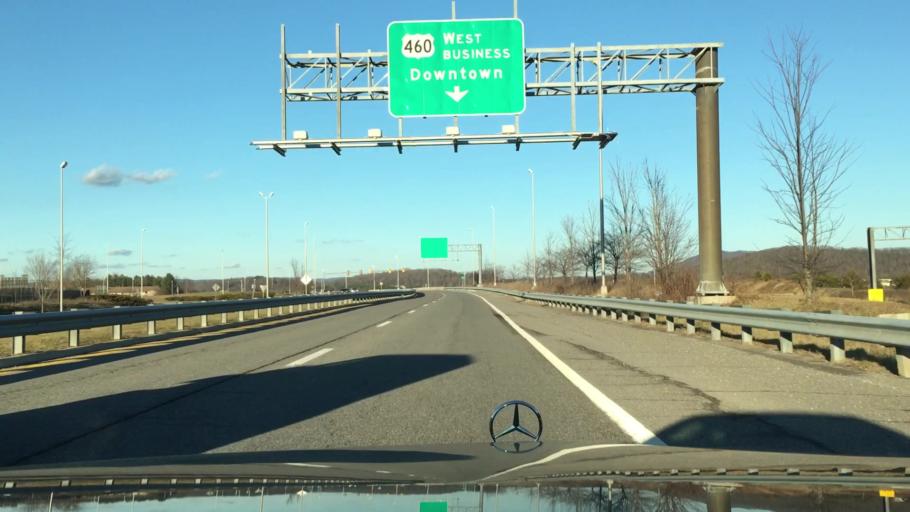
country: US
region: Virginia
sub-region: Montgomery County
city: Merrimac
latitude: 37.1897
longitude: -80.4053
